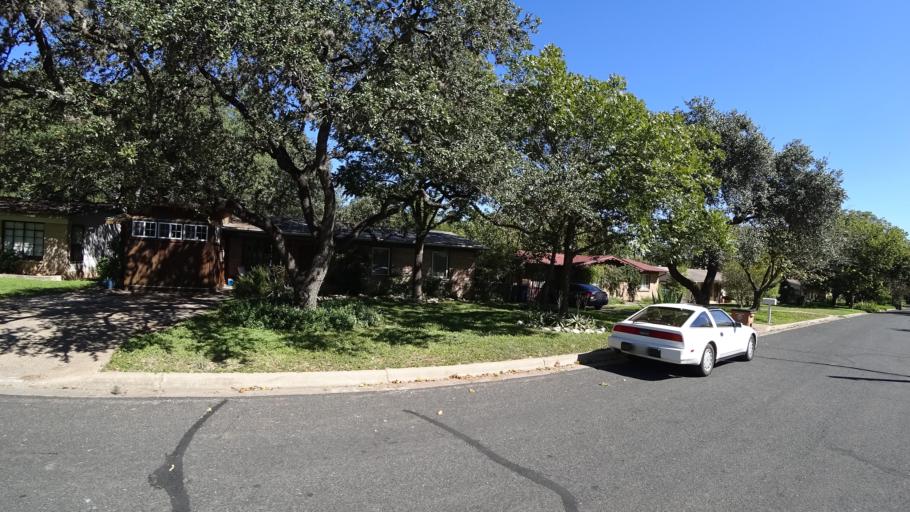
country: US
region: Texas
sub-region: Travis County
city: Austin
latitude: 30.2433
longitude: -97.7673
